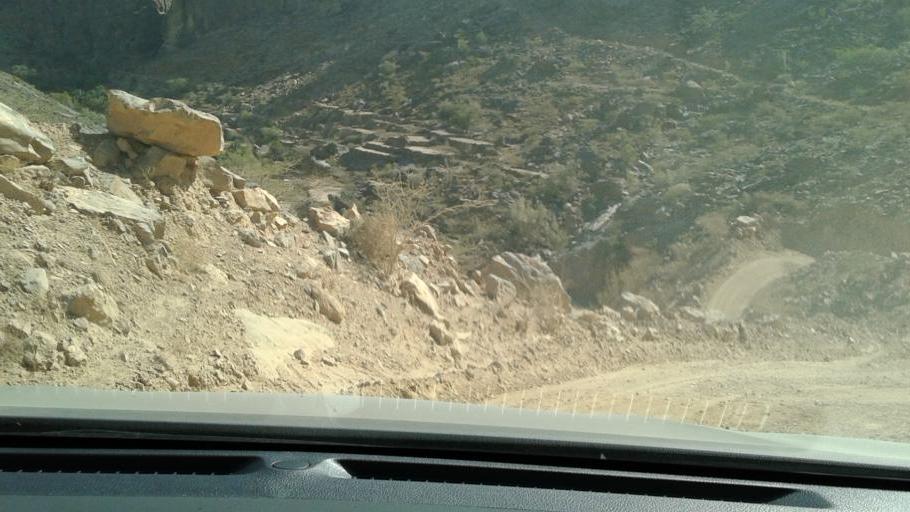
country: OM
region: Al Batinah
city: Bayt al `Awabi
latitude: 23.1990
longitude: 57.3904
